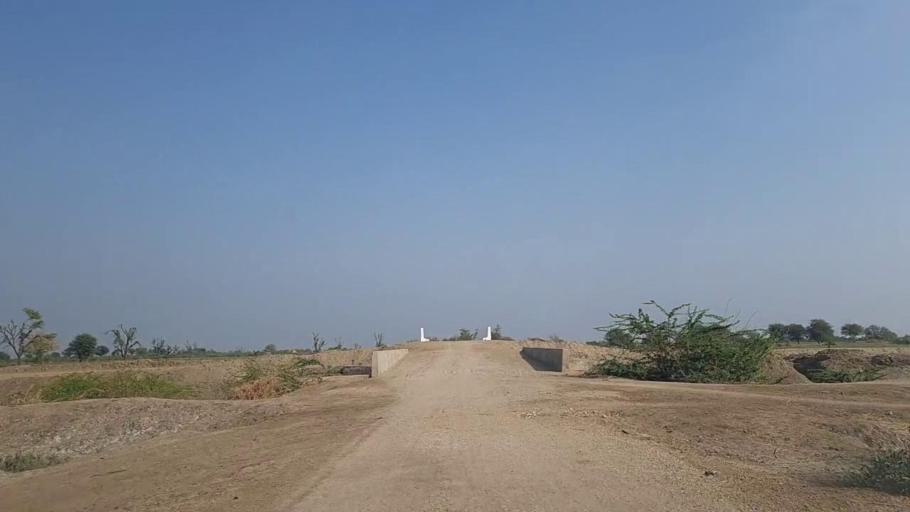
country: PK
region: Sindh
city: Dhoro Naro
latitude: 25.4865
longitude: 69.5409
